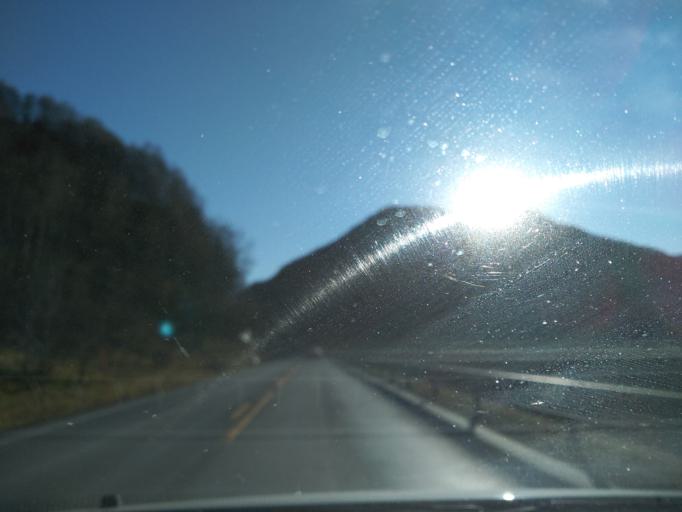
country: NO
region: Hordaland
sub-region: Etne
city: Etne
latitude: 59.7416
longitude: 6.1220
